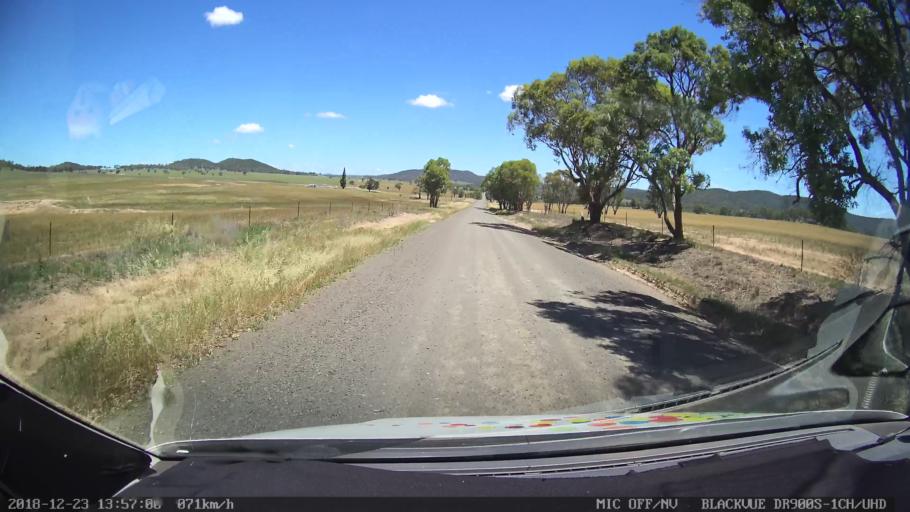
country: AU
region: New South Wales
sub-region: Tamworth Municipality
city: Manilla
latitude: -30.5833
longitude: 151.0943
